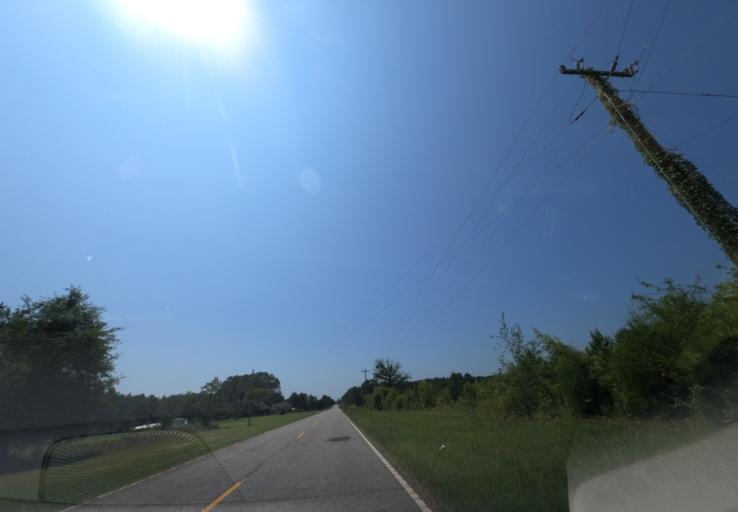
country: US
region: South Carolina
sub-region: Greenwood County
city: Greenwood
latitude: 34.0240
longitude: -82.1278
